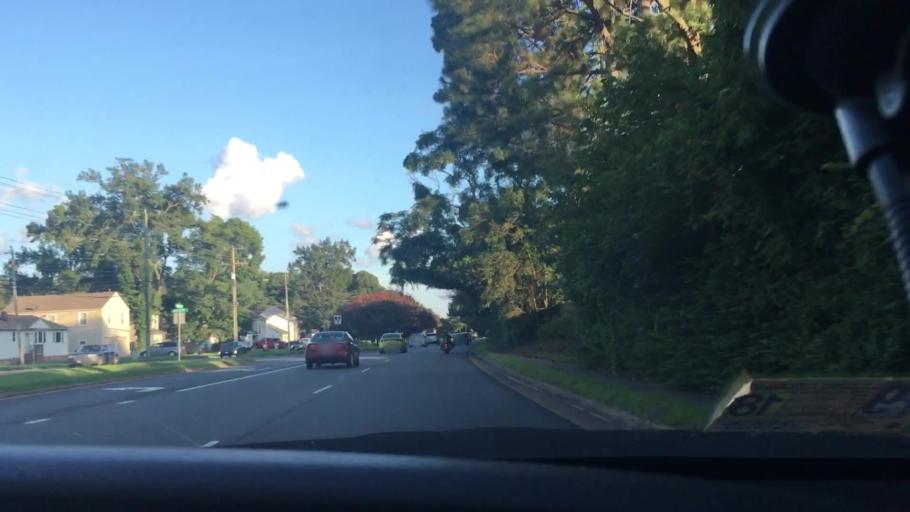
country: US
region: Virginia
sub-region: City of Norfolk
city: Norfolk
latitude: 36.8914
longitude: -76.1392
